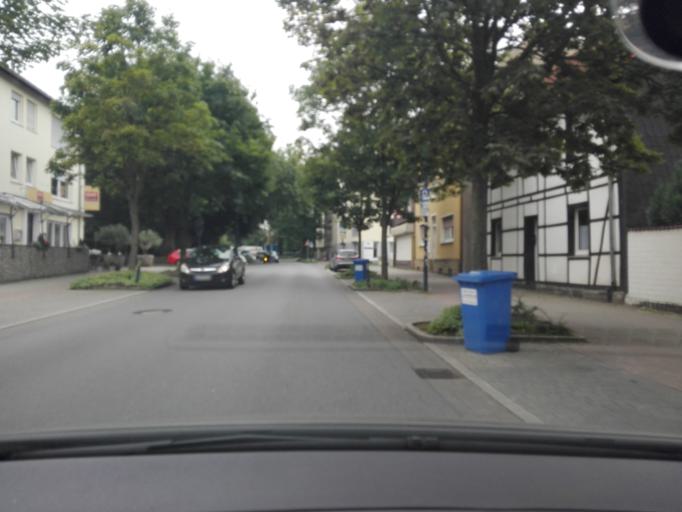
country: DE
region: North Rhine-Westphalia
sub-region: Regierungsbezirk Arnsberg
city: Holzwickede
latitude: 51.5000
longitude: 7.6159
